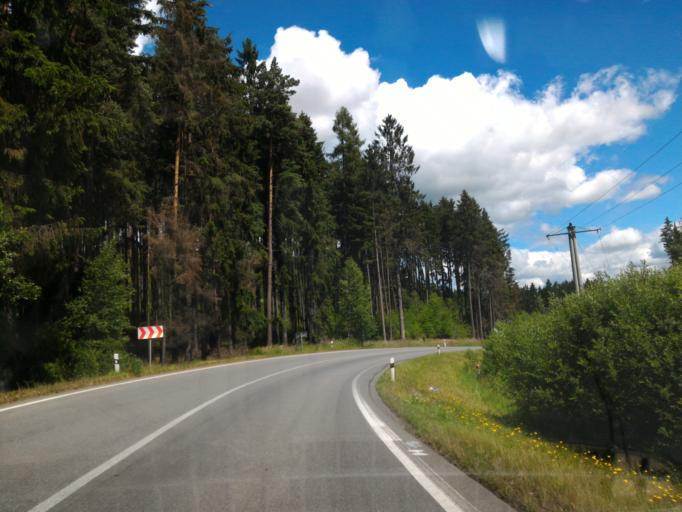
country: CZ
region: Vysocina
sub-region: Okres Jihlava
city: Trest'
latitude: 49.2500
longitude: 15.4687
